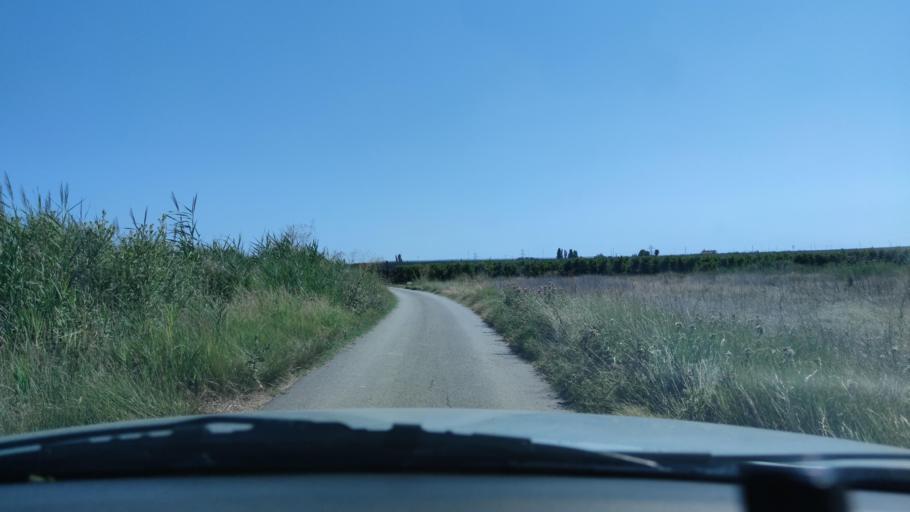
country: ES
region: Catalonia
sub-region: Provincia de Lleida
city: Alcoletge
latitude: 41.6712
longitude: 0.6614
